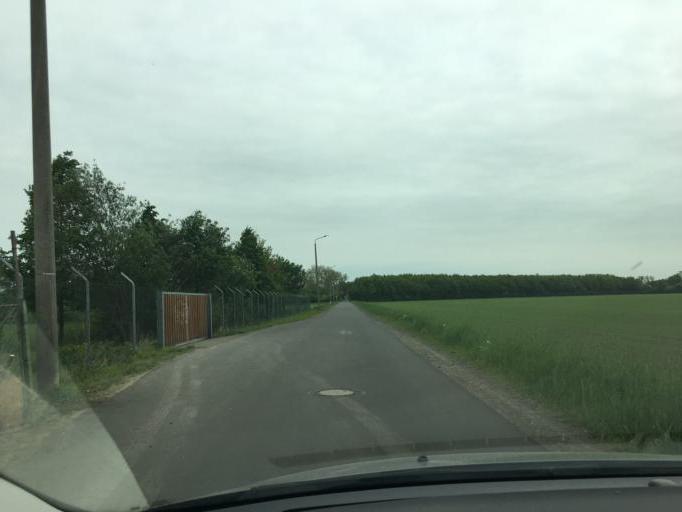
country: DE
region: Saxony
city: Taucha
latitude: 51.3707
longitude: 12.4448
